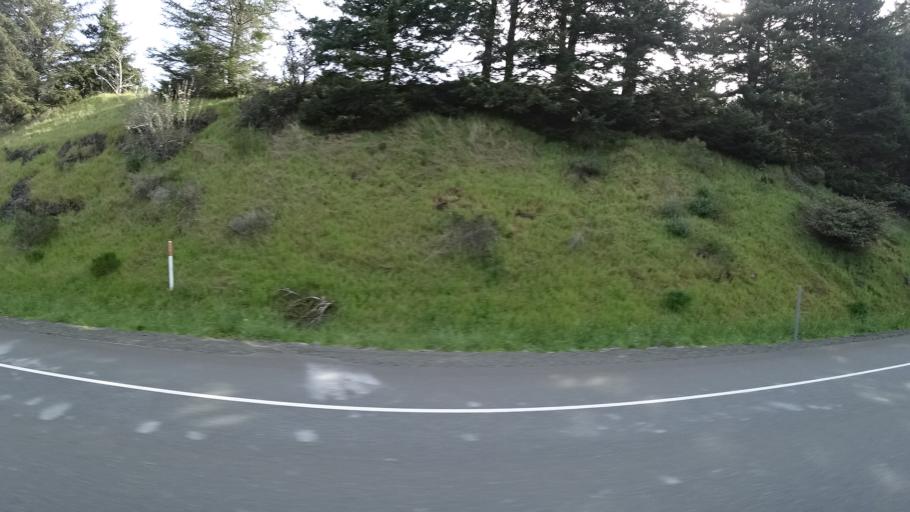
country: US
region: Oregon
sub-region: Curry County
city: Gold Beach
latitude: 42.3657
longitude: -124.4181
